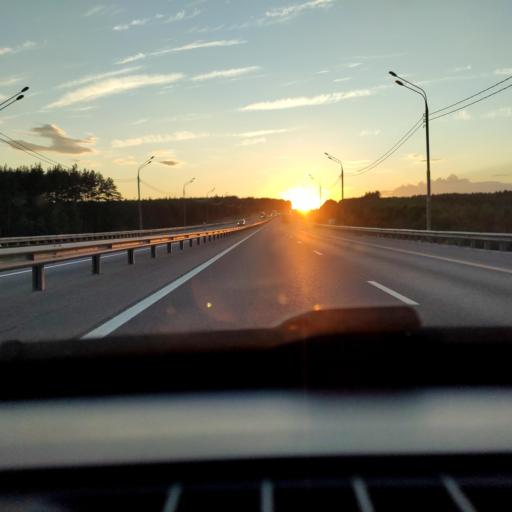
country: RU
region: Lipetsk
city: Khlevnoye
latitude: 52.2244
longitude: 39.1078
